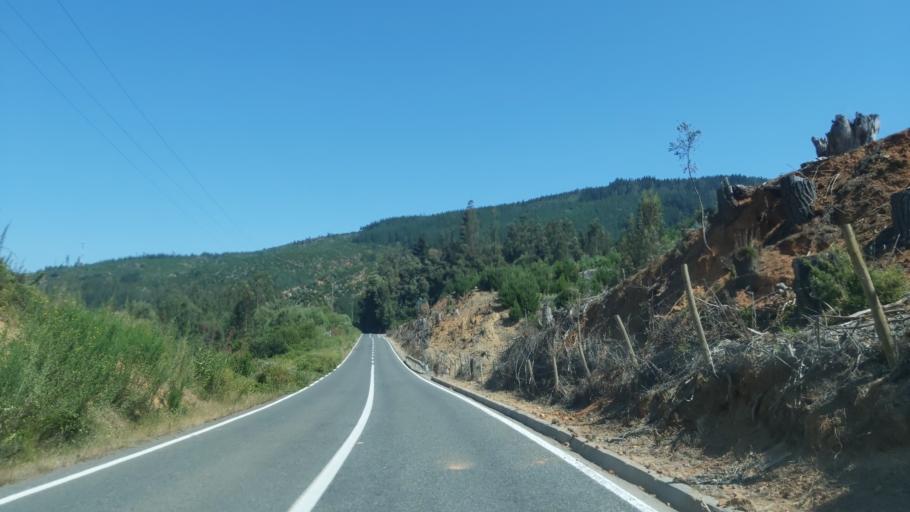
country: CL
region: Biobio
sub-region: Provincia de Concepcion
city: Tome
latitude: -36.5493
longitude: -72.8795
